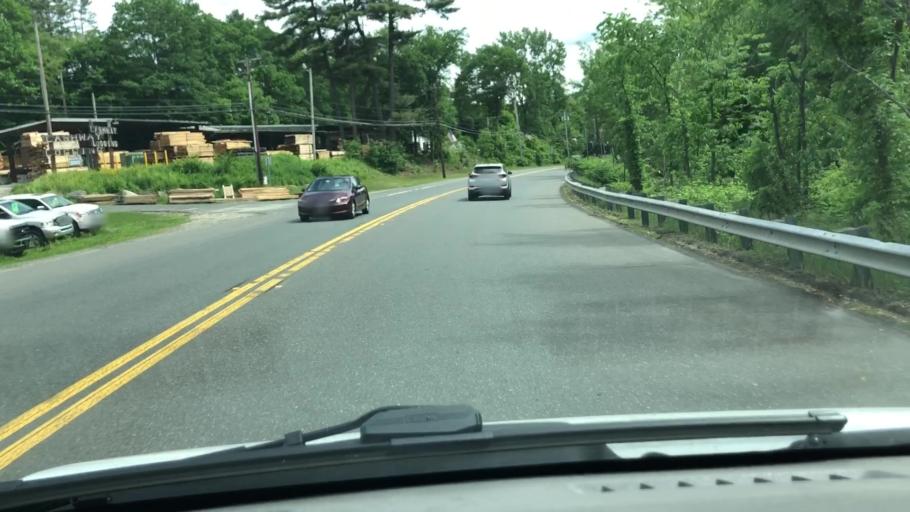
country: US
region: Massachusetts
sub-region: Hampshire County
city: Williamsburg
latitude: 42.3872
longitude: -72.7175
